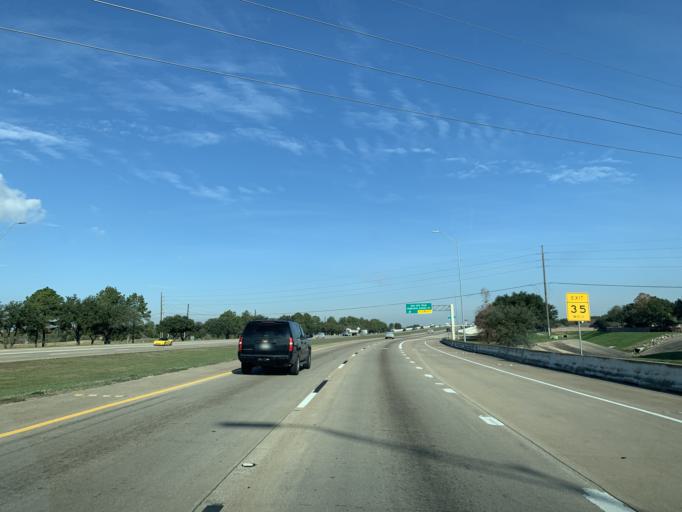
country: US
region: Texas
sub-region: Fort Bend County
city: Cinco Ranch
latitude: 29.7514
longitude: -95.7757
